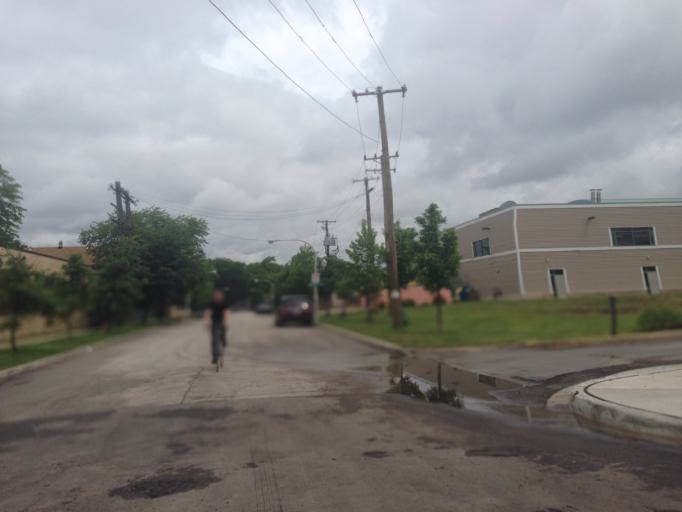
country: US
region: Illinois
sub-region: Cook County
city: Oak Park
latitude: 41.9140
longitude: -87.7203
